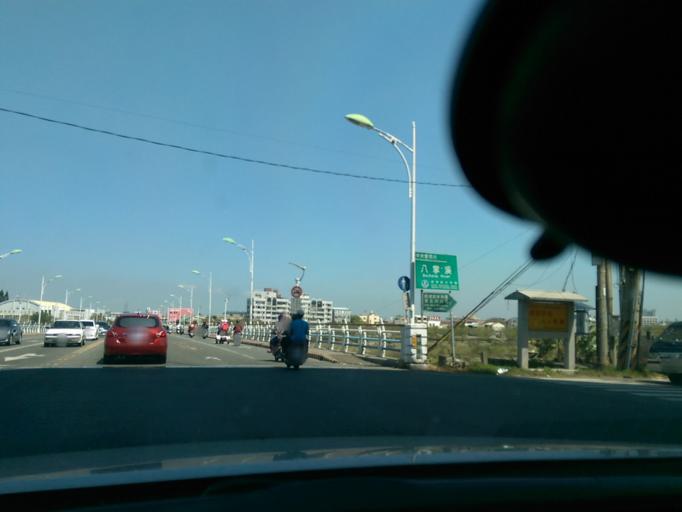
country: TW
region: Taiwan
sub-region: Chiayi
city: Jiayi Shi
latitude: 23.4569
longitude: 120.4587
